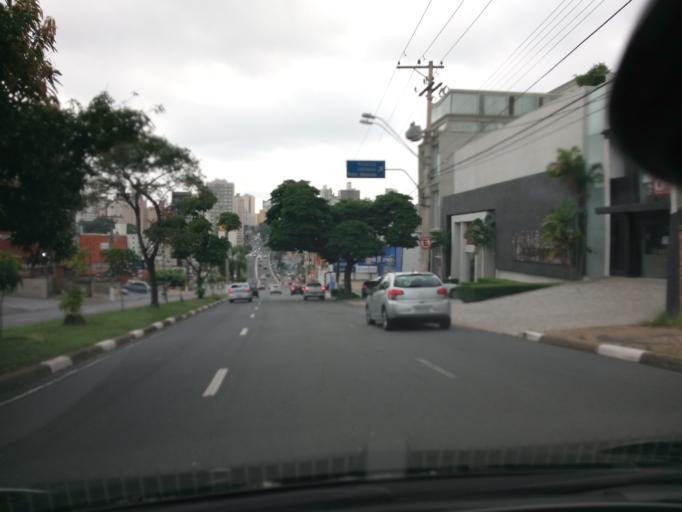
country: BR
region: Sao Paulo
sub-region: Campinas
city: Campinas
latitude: -22.9064
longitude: -47.0433
